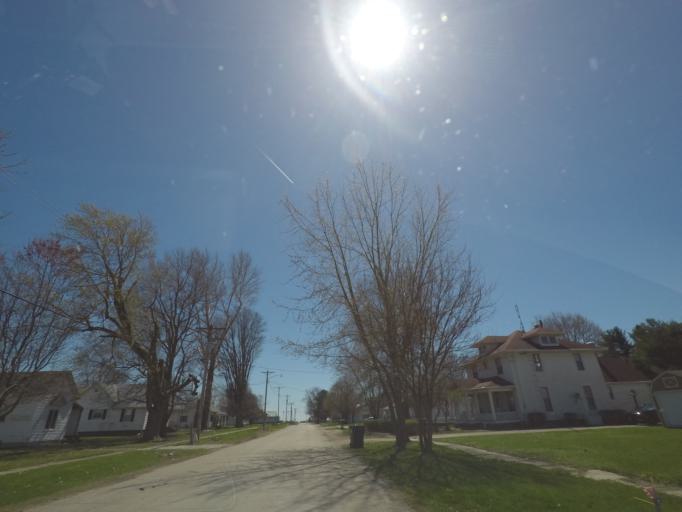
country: US
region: Illinois
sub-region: Macon County
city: Warrensburg
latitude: 39.9642
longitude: -89.1627
